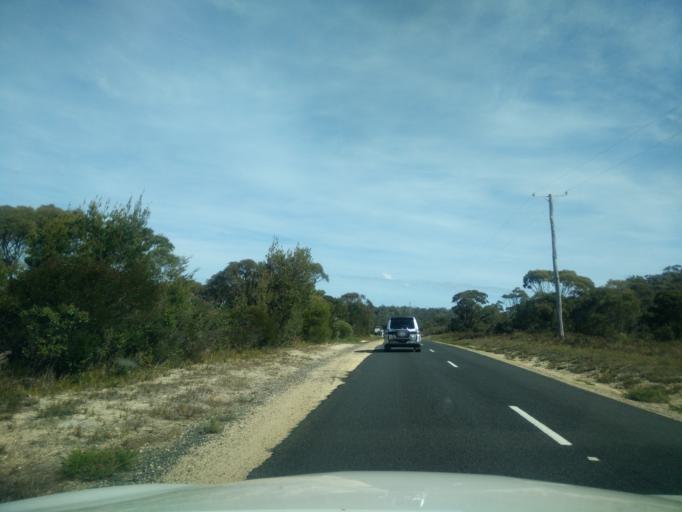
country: AU
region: Tasmania
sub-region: Break O'Day
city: St Helens
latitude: -41.2340
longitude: 148.2837
